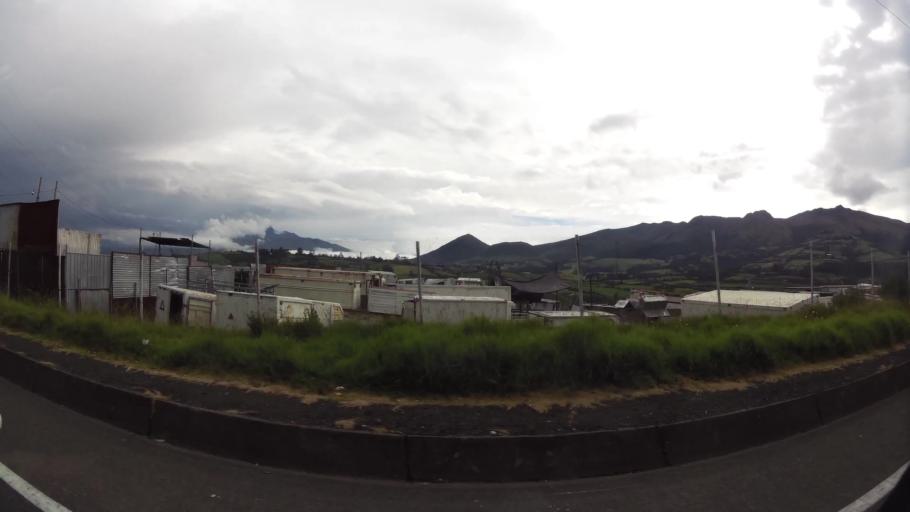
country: EC
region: Pichincha
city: Sangolqui
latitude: -0.3837
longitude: -78.5509
